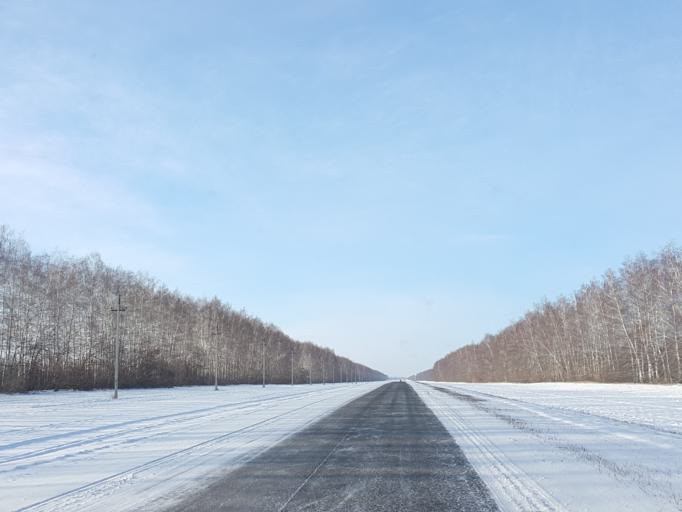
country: RU
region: Tambov
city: Znamenka
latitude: 52.3720
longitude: 41.2923
